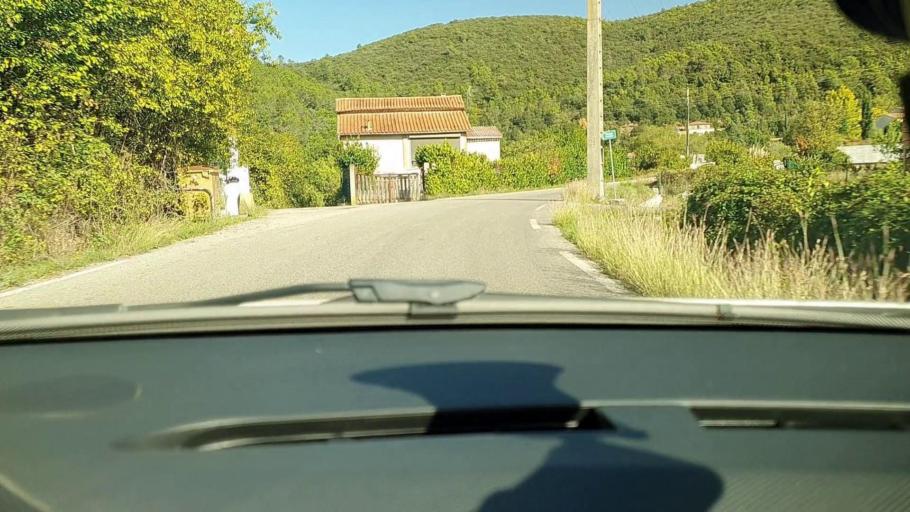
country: FR
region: Languedoc-Roussillon
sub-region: Departement du Gard
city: Saint-Florent-sur-Auzonnet
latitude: 44.2422
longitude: 4.1167
